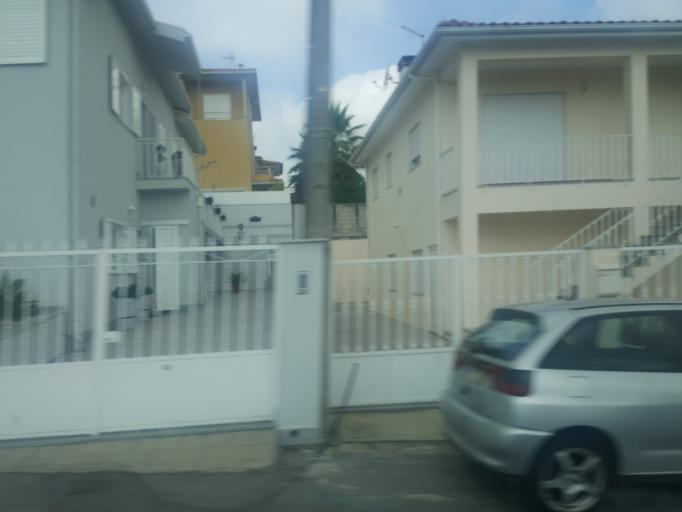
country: PT
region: Porto
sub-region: Marco de Canaveses
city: Marco de Canavezes
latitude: 41.1960
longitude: -8.1857
